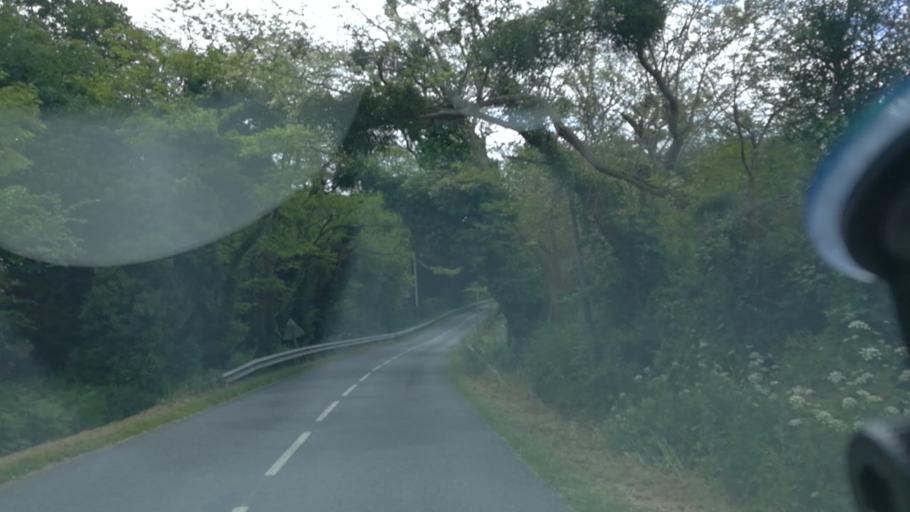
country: FR
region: Brittany
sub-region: Departement du Morbihan
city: Penestin
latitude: 47.4642
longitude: -2.4268
